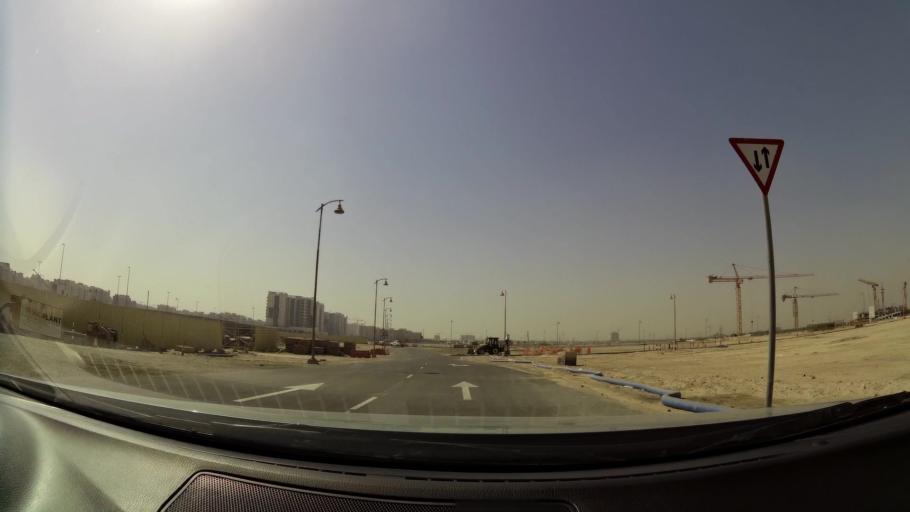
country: AE
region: Dubai
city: Dubai
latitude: 25.0359
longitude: 55.1418
